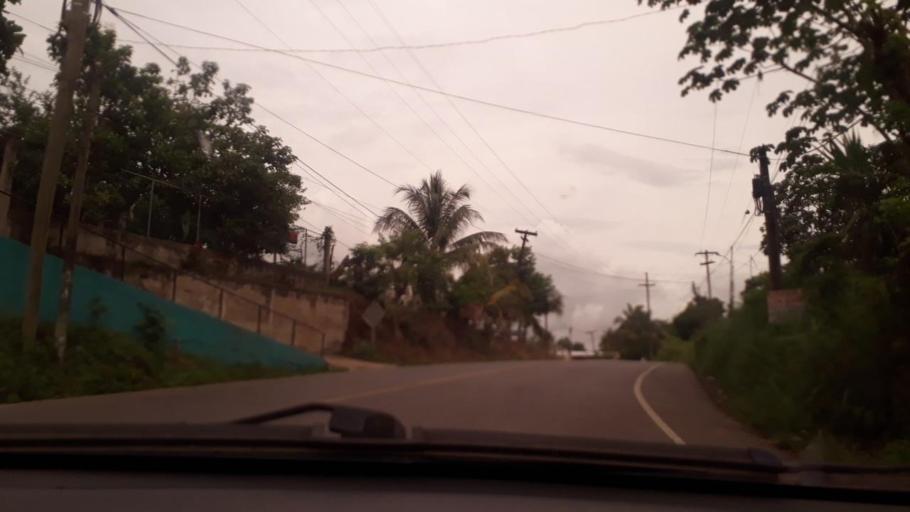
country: GT
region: Izabal
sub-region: Municipio de Puerto Barrios
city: Puerto Barrios
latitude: 15.6396
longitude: -88.5458
